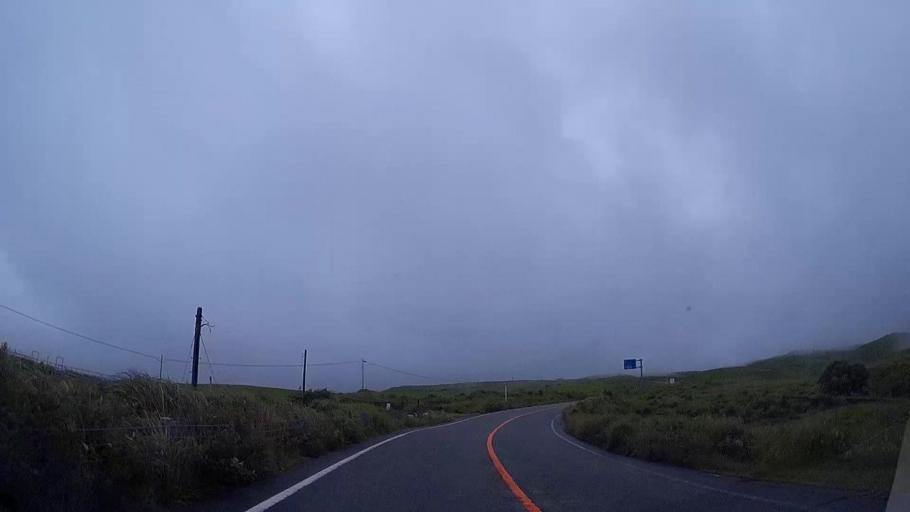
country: JP
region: Kumamoto
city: Aso
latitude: 33.0083
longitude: 131.0691
